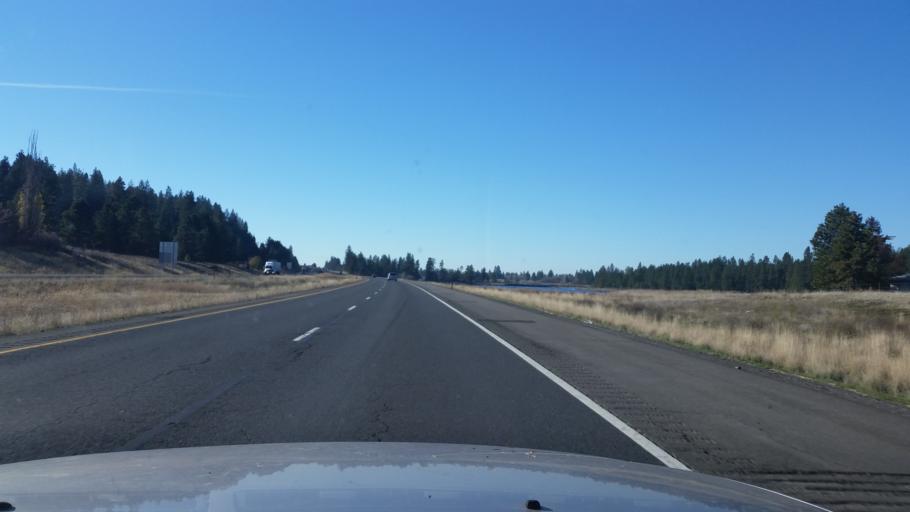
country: US
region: Washington
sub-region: Spokane County
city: Fairchild Air Force Base
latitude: 47.5585
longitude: -117.6105
